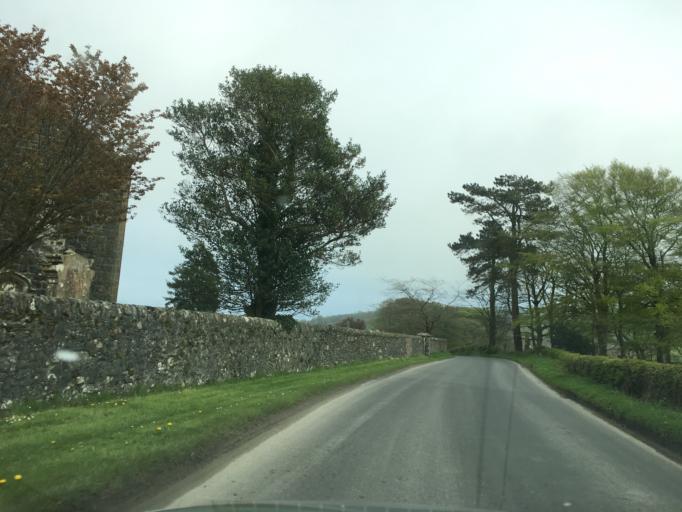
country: GB
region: Scotland
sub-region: Argyll and Bute
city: Port Bannatyne
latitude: 55.8597
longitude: -5.1129
